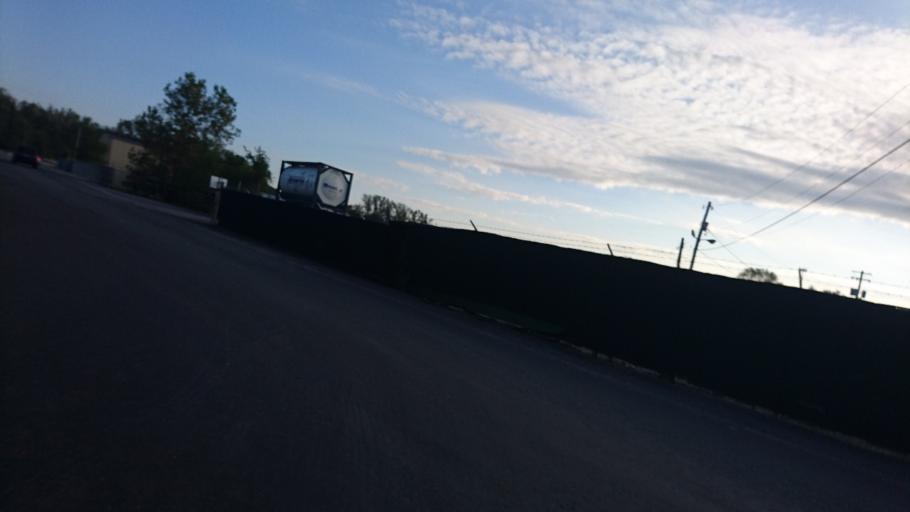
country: US
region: Illinois
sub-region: Madison County
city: Mitchell
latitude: 38.7603
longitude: -90.1151
